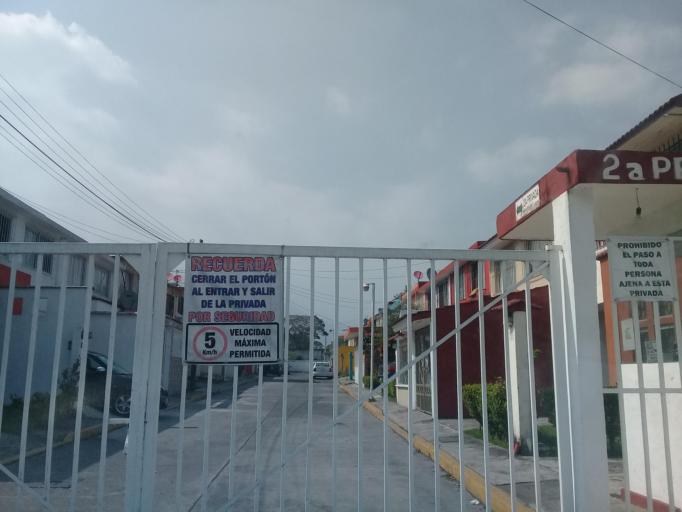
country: MX
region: Veracruz
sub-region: Mariano Escobedo
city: Palmira
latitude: 18.8757
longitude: -97.1054
